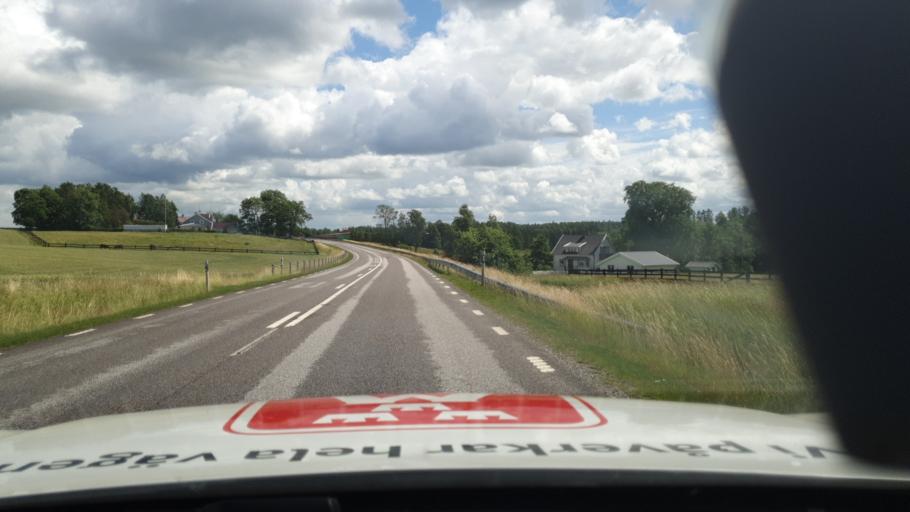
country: SE
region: Vaestra Goetaland
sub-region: Vara Kommun
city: Kvanum
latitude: 58.2263
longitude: 13.1594
